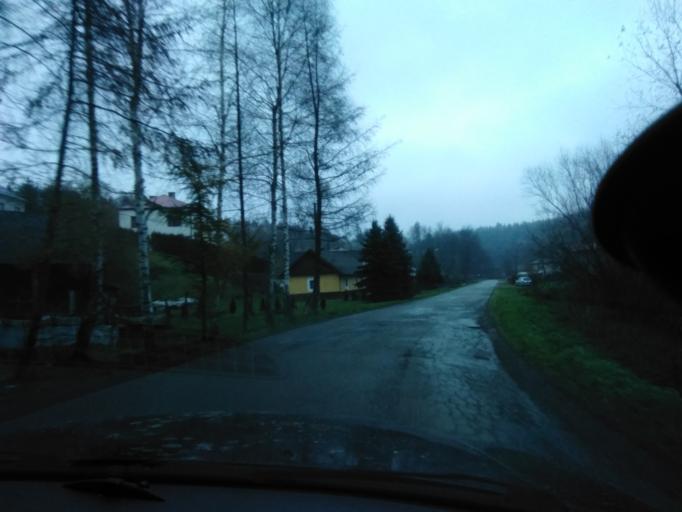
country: PL
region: Subcarpathian Voivodeship
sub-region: Powiat brzozowski
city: Nozdrzec
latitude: 49.7556
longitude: 22.1458
